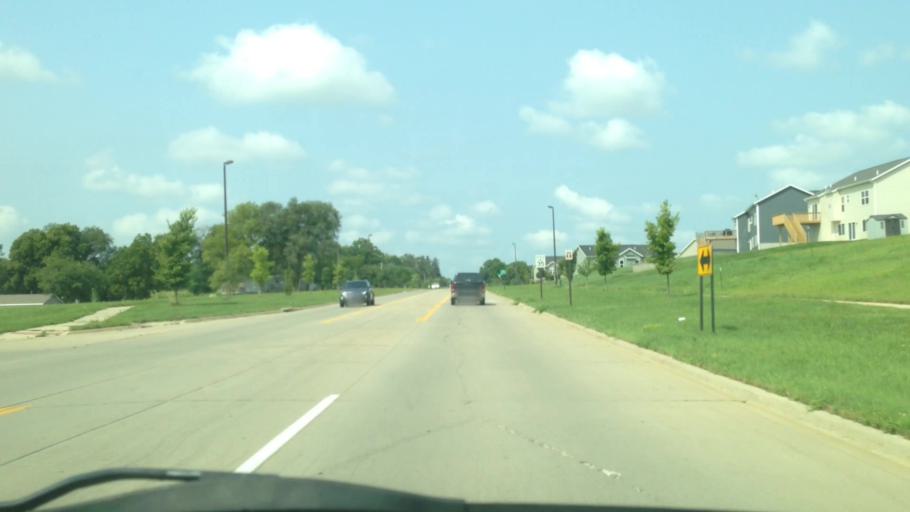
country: US
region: Iowa
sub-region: Linn County
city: Cedar Rapids
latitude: 41.9456
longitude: -91.7000
